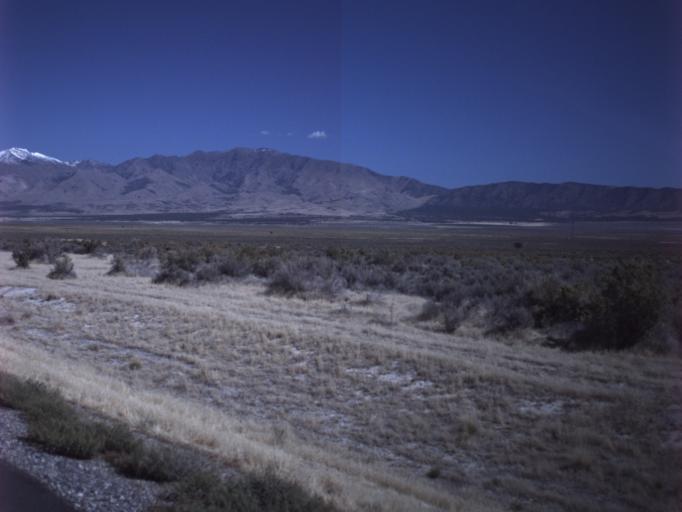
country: US
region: Utah
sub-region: Tooele County
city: Grantsville
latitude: 40.2417
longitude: -112.7232
